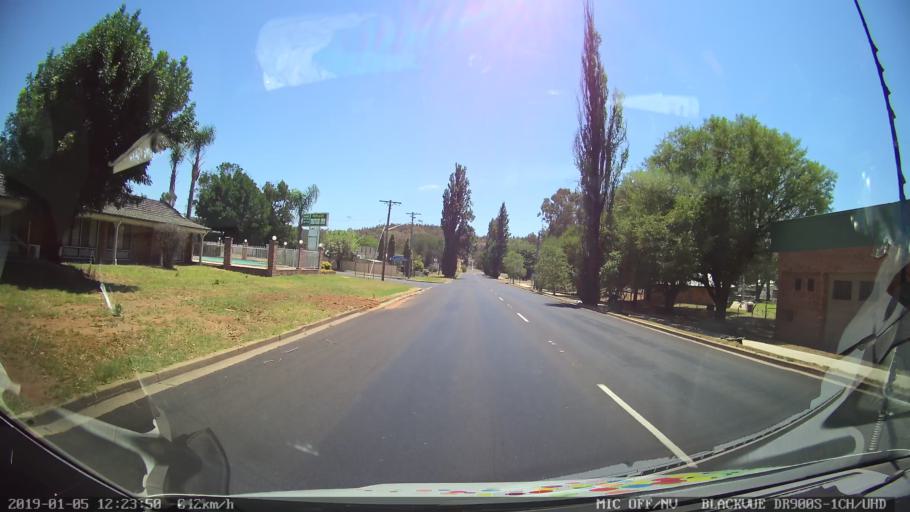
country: AU
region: New South Wales
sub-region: Warrumbungle Shire
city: Coonabarabran
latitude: -31.2688
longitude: 149.2763
